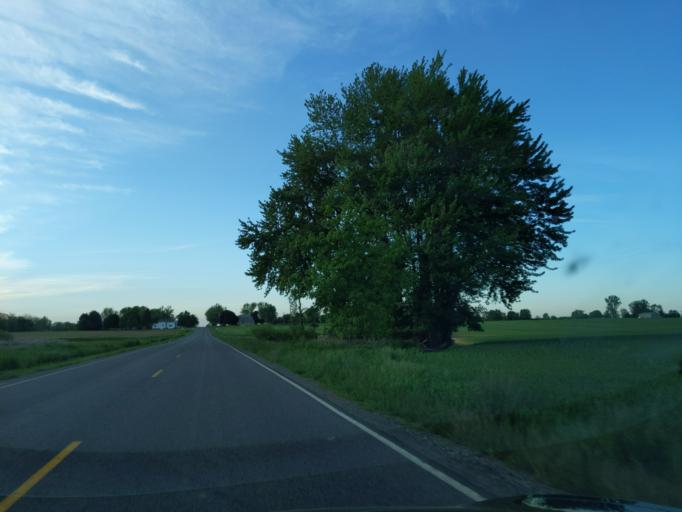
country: US
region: Michigan
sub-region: Ingham County
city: Williamston
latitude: 42.5790
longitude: -84.2985
